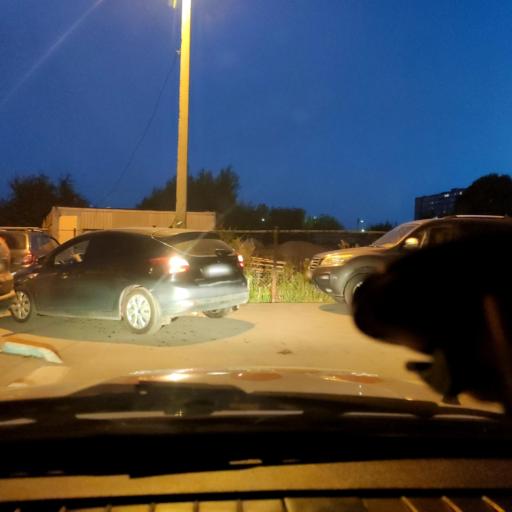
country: RU
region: Voronezj
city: Novaya Usman'
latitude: 51.6098
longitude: 39.3824
